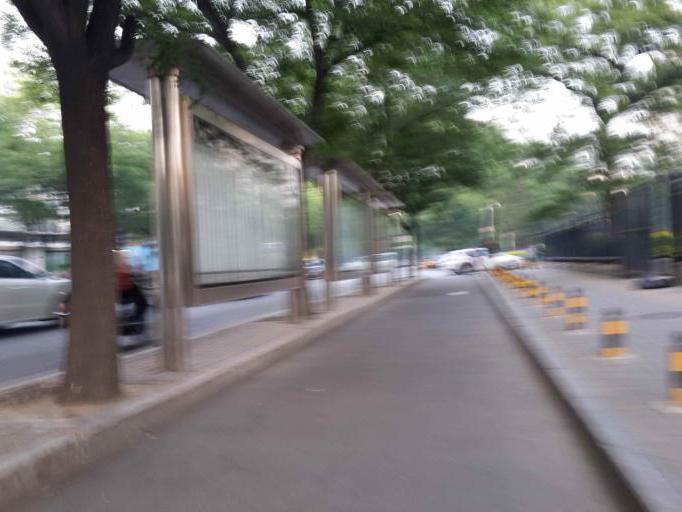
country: CN
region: Beijing
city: Chaowai
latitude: 39.9255
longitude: 116.4402
